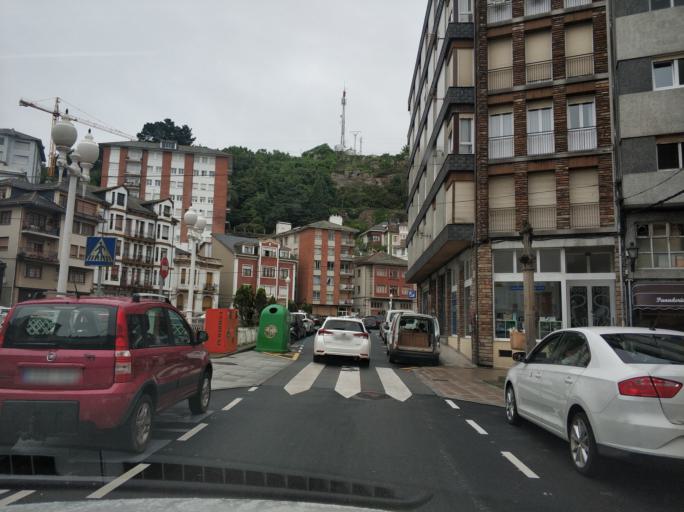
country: ES
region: Asturias
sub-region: Province of Asturias
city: Navia
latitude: 43.5439
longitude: -6.5346
